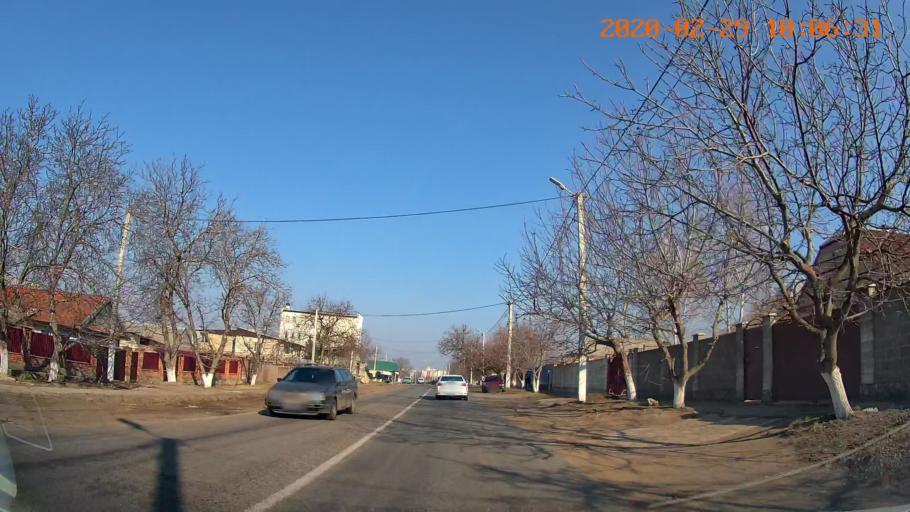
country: MD
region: Telenesti
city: Tiraspolul Nou
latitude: 46.8152
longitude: 29.6691
